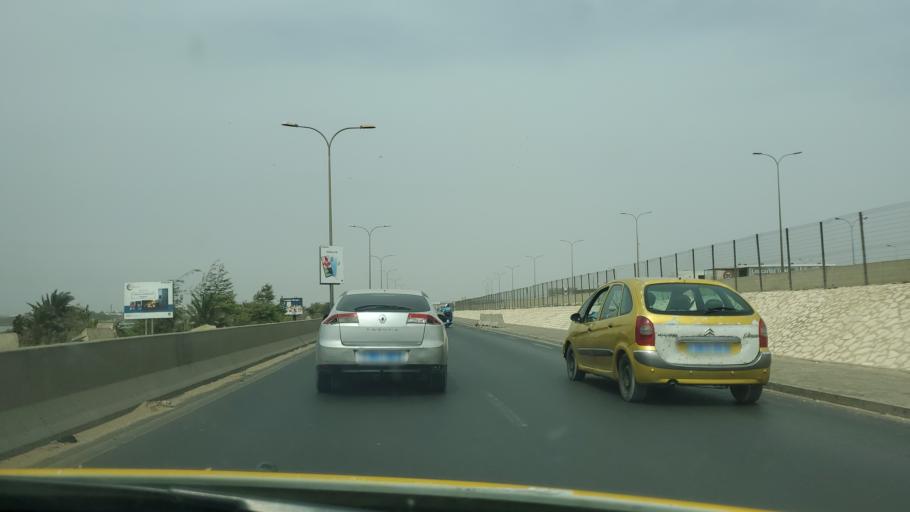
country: SN
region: Dakar
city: Pikine
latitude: 14.7457
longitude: -17.4202
